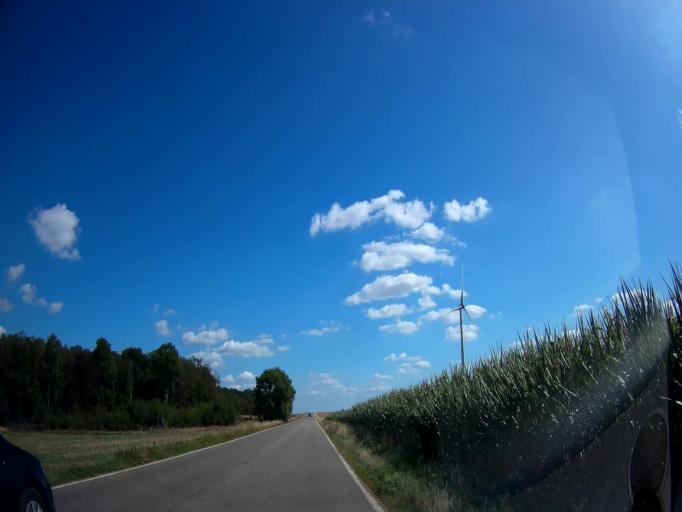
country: BE
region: Wallonia
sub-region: Province de Namur
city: Hastiere-Lavaux
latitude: 50.1808
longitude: 4.8583
